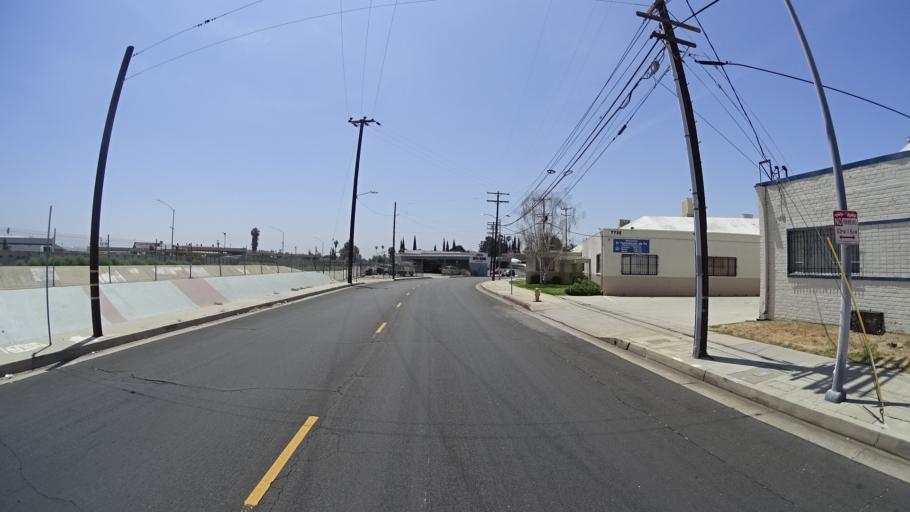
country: US
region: California
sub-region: Los Angeles County
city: Van Nuys
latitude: 34.2120
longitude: -118.4579
